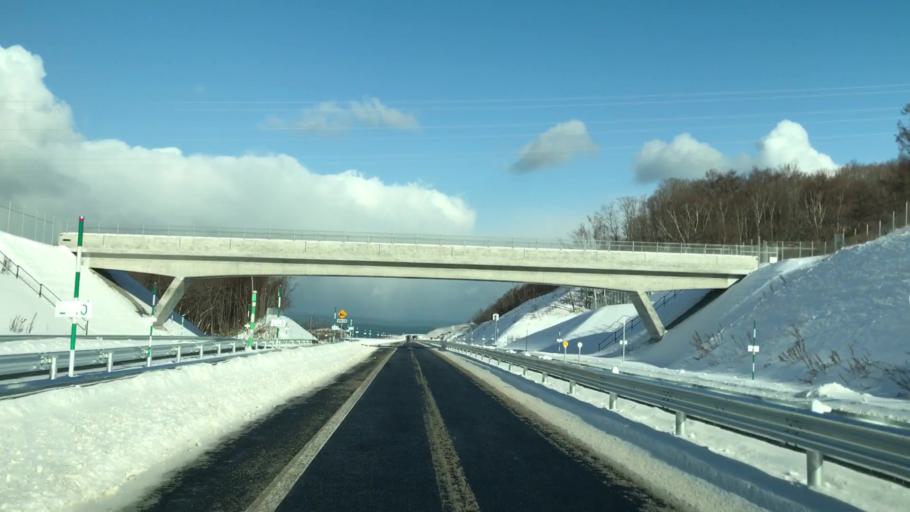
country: JP
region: Hokkaido
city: Otaru
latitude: 43.1631
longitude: 141.0582
